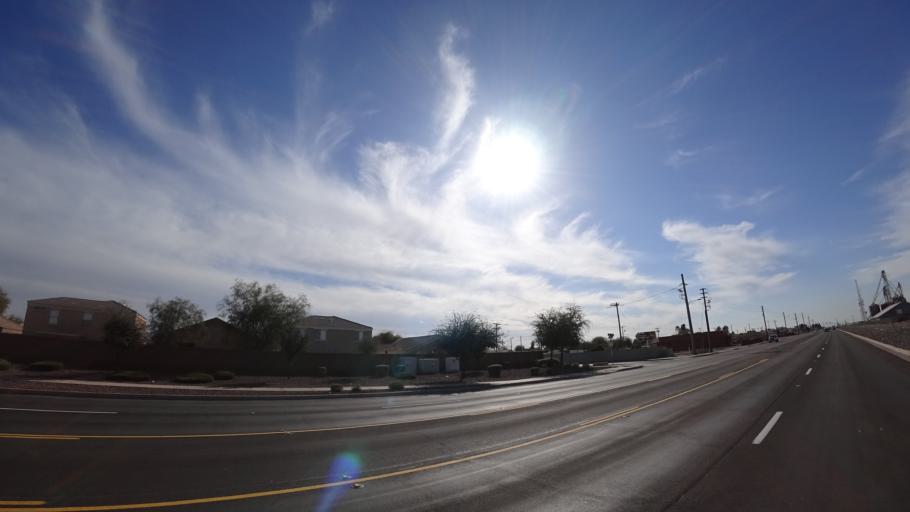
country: US
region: Arizona
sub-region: Maricopa County
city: Tolleson
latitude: 33.4355
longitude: -112.2932
